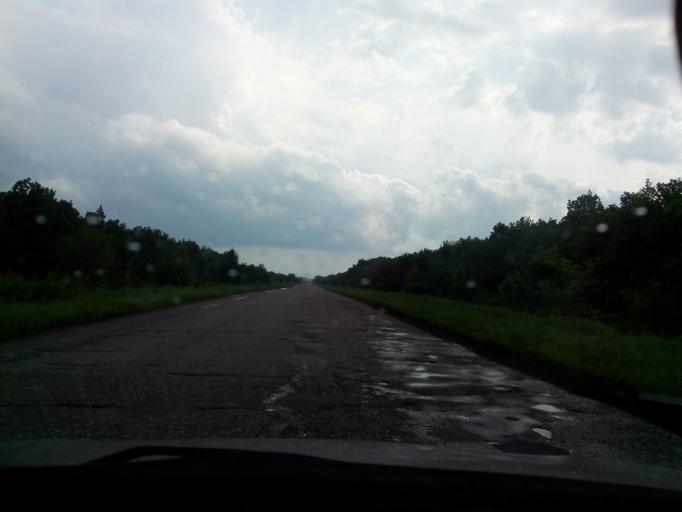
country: RU
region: Volgograd
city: Kumylzhenskaya
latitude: 49.9058
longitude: 42.9180
